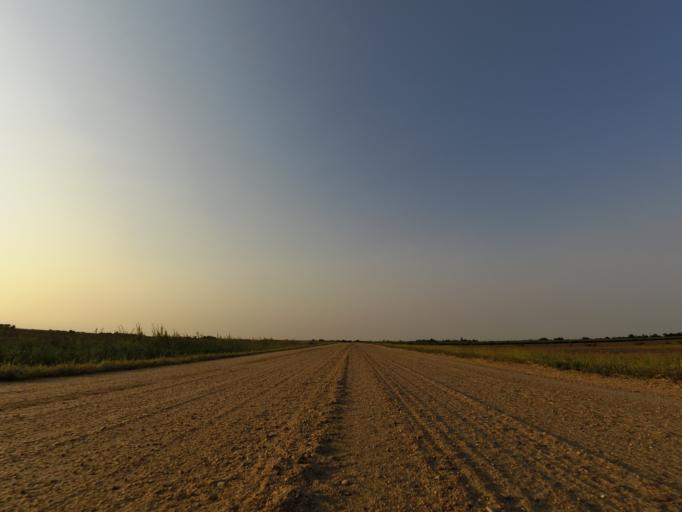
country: US
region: Kansas
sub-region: Reno County
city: South Hutchinson
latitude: 37.9704
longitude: -97.9957
